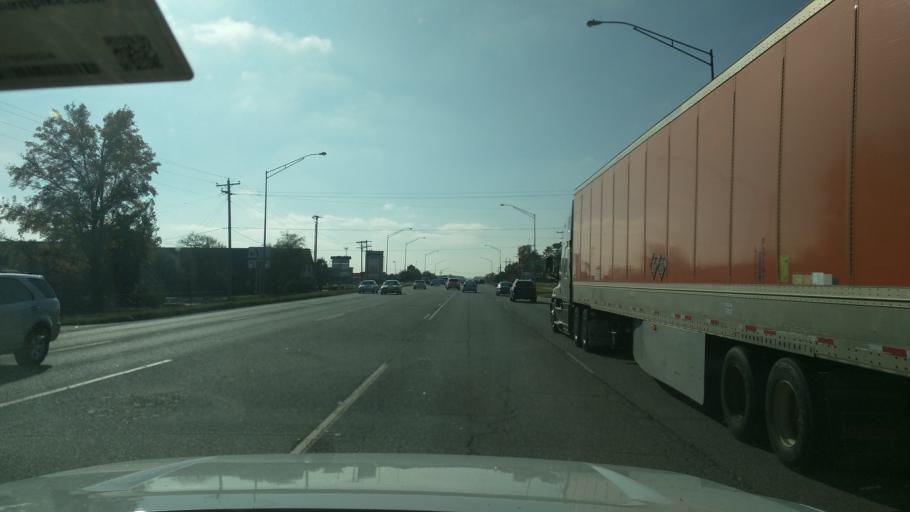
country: US
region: Oklahoma
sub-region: Washington County
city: Bartlesville
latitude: 36.7188
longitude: -95.9352
